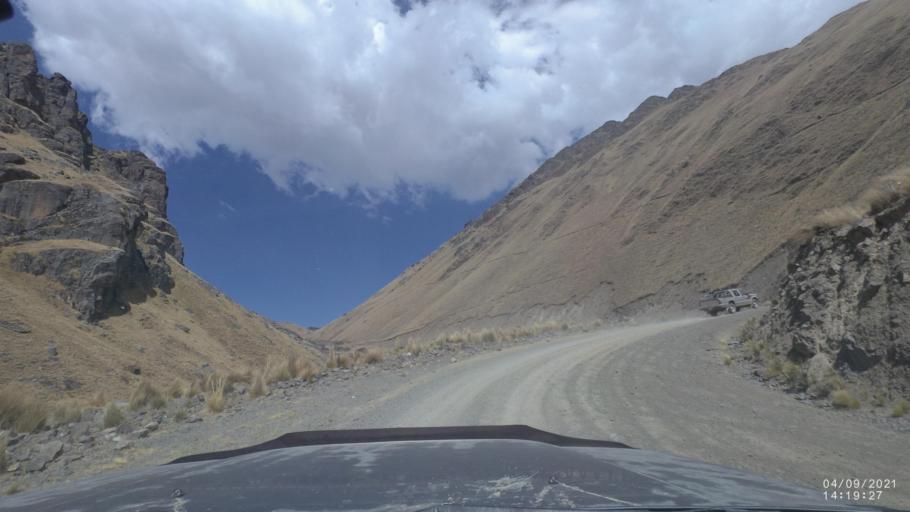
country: BO
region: Cochabamba
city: Sipe Sipe
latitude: -17.2325
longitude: -66.4232
